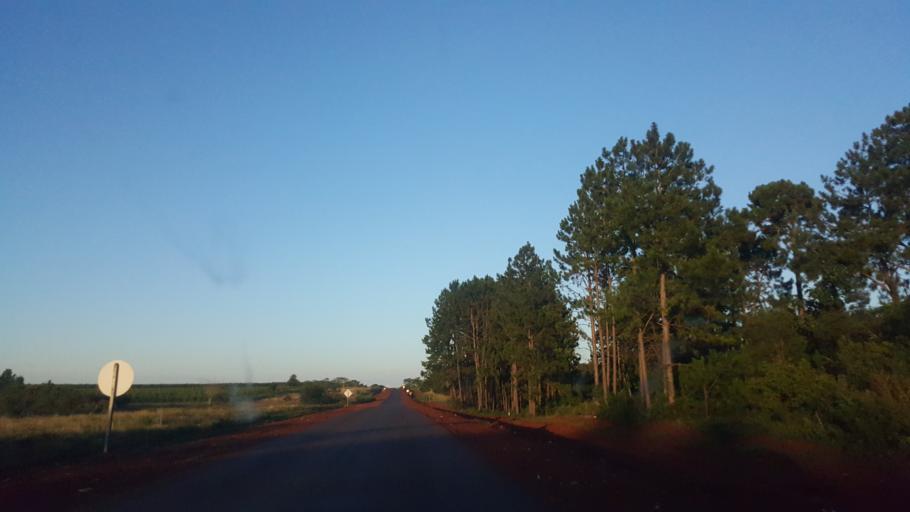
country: AR
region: Corrientes
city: Santo Tome
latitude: -28.5045
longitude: -56.0569
